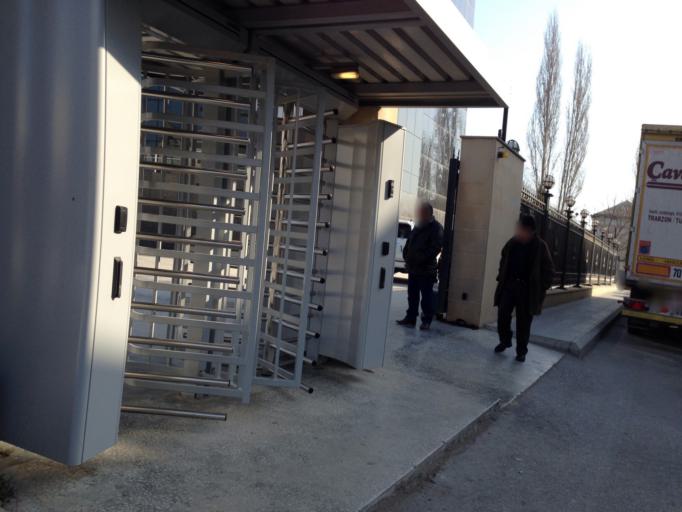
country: AZ
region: Baki
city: Baku
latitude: 40.3961
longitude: 49.8793
